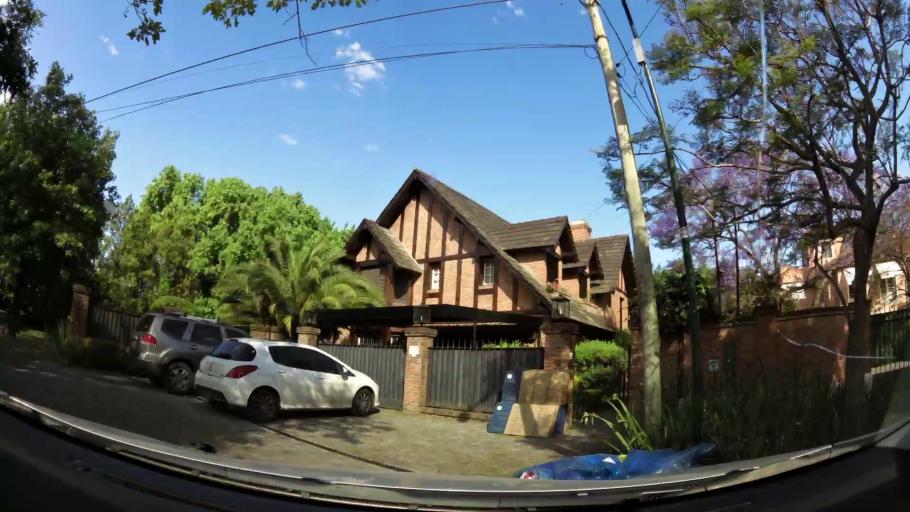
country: AR
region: Buenos Aires
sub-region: Partido de San Isidro
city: San Isidro
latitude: -34.4864
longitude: -58.5663
